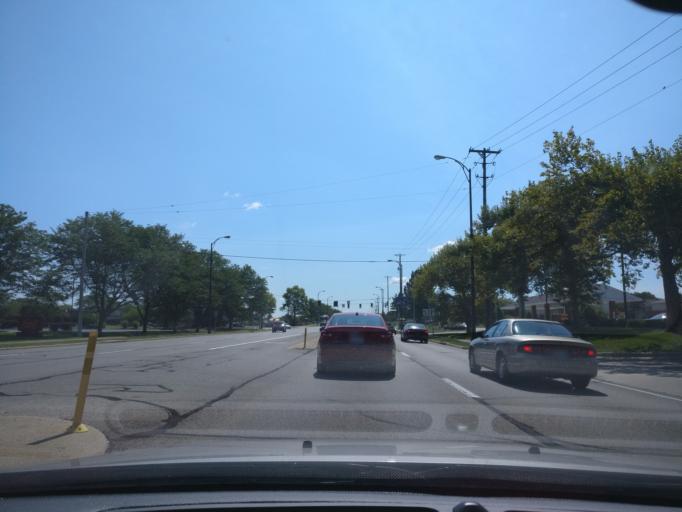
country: US
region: Ohio
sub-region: Montgomery County
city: Centerville
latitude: 39.6299
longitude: -84.1946
